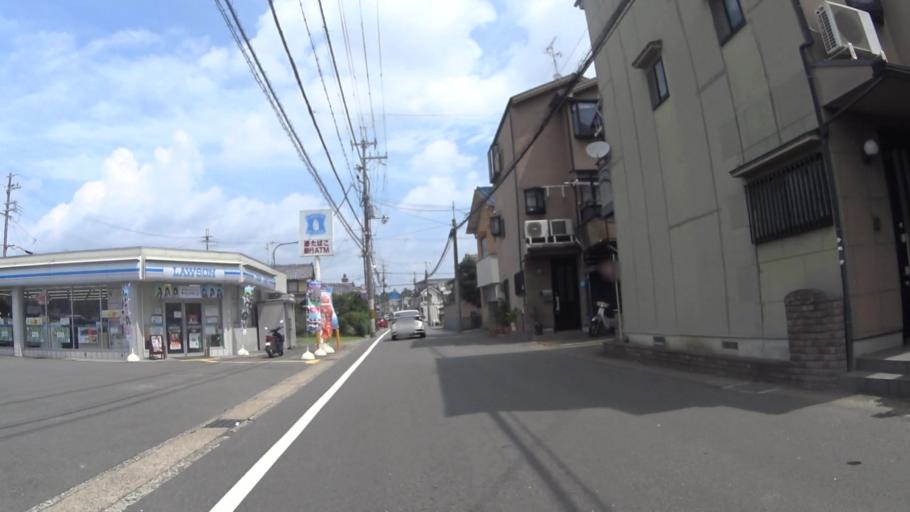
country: JP
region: Kyoto
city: Muko
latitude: 34.9433
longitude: 135.7331
